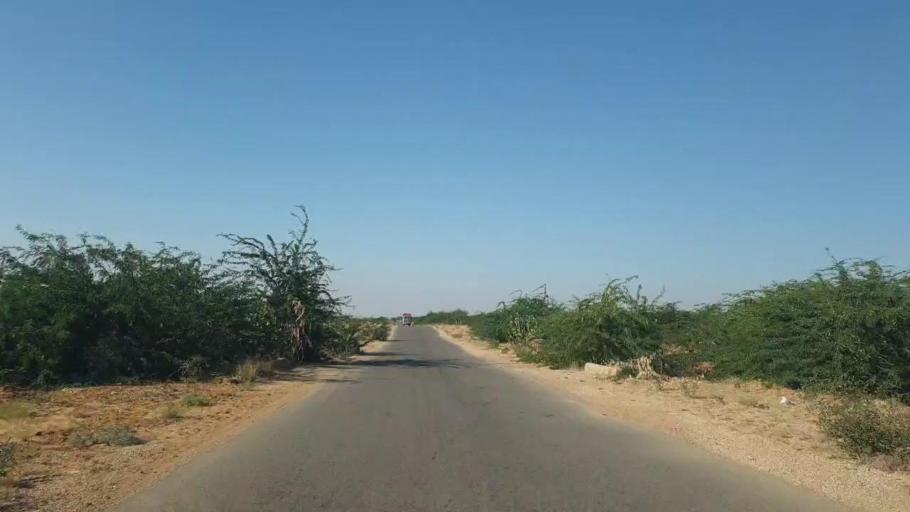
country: PK
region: Sindh
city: Malir Cantonment
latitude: 25.2670
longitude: 67.5955
